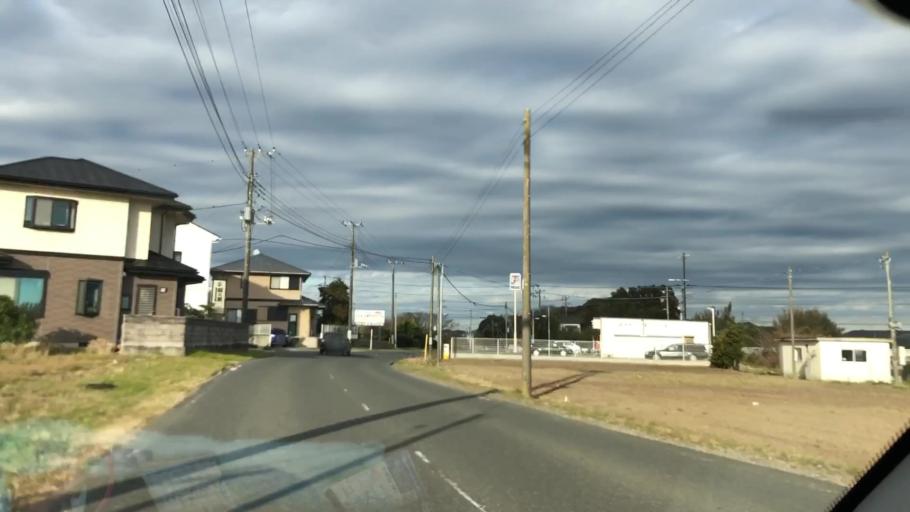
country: JP
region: Chiba
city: Tateyama
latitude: 35.0061
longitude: 139.8812
